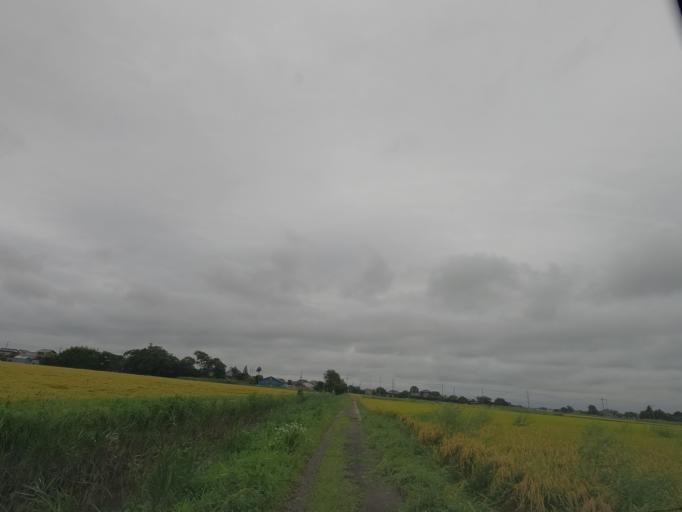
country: JP
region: Ibaraki
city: Toride
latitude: 35.9253
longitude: 140.0697
